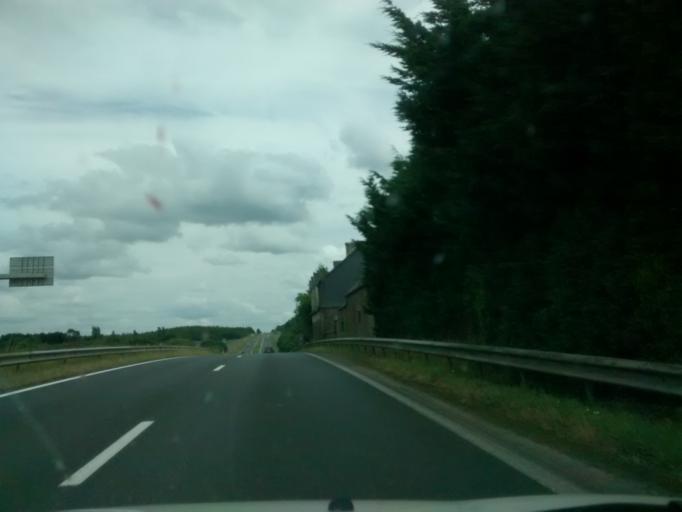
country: FR
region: Brittany
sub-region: Departement des Cotes-d'Armor
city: Saint-Agathon
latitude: 48.5433
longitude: -3.0825
